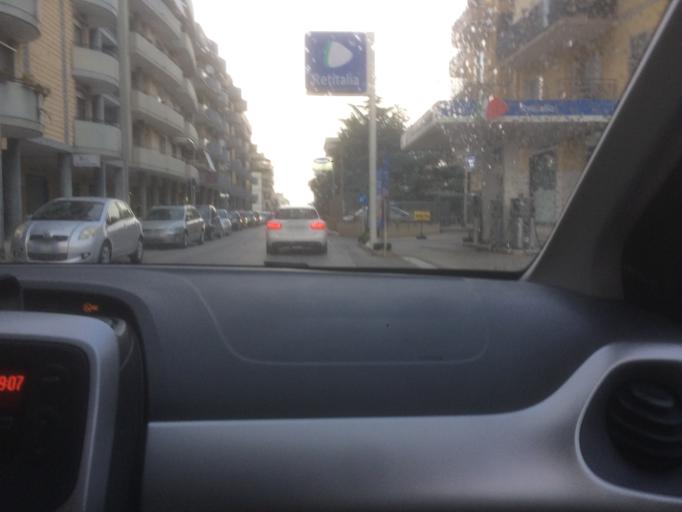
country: IT
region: Apulia
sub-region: Provincia di Bari
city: Triggiano
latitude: 41.0675
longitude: 16.9326
